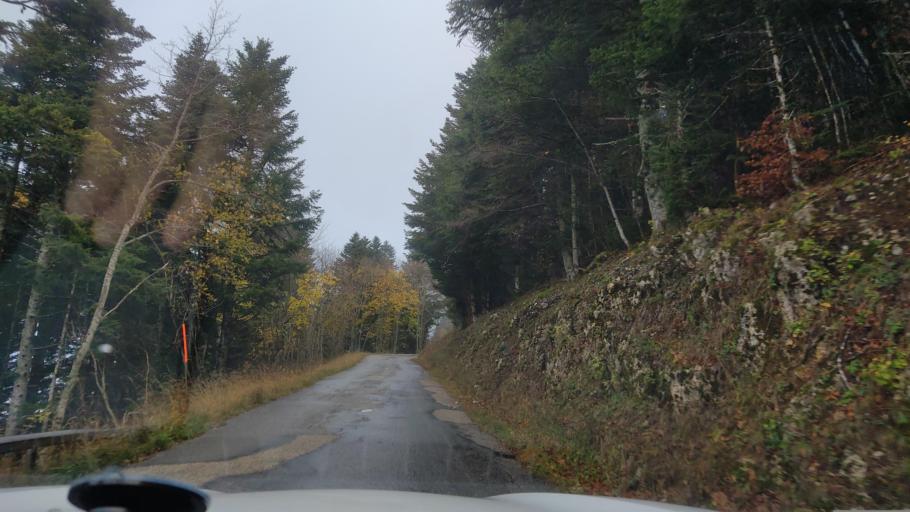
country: FR
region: Rhone-Alpes
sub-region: Departement de la Savoie
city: Le Bourget-du-Lac
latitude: 45.6521
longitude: 5.8099
